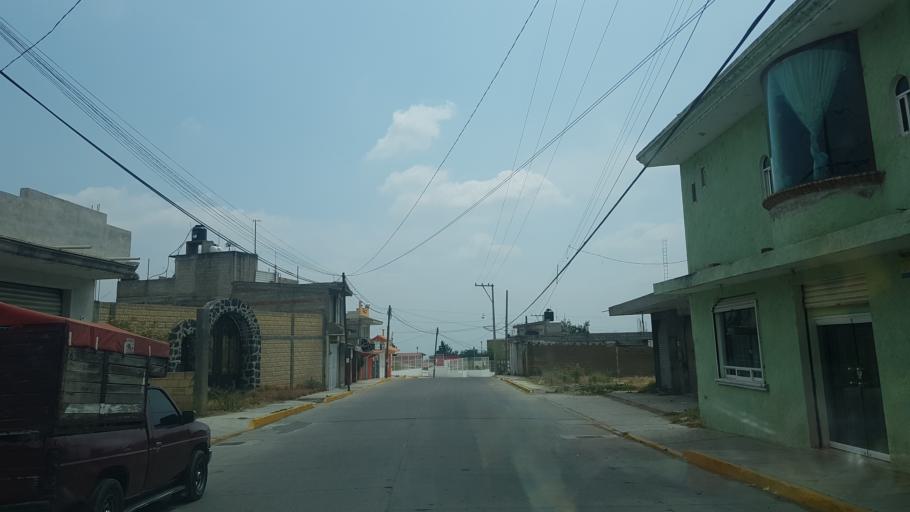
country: MX
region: Puebla
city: Domingo Arenas
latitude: 19.1394
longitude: -98.4501
